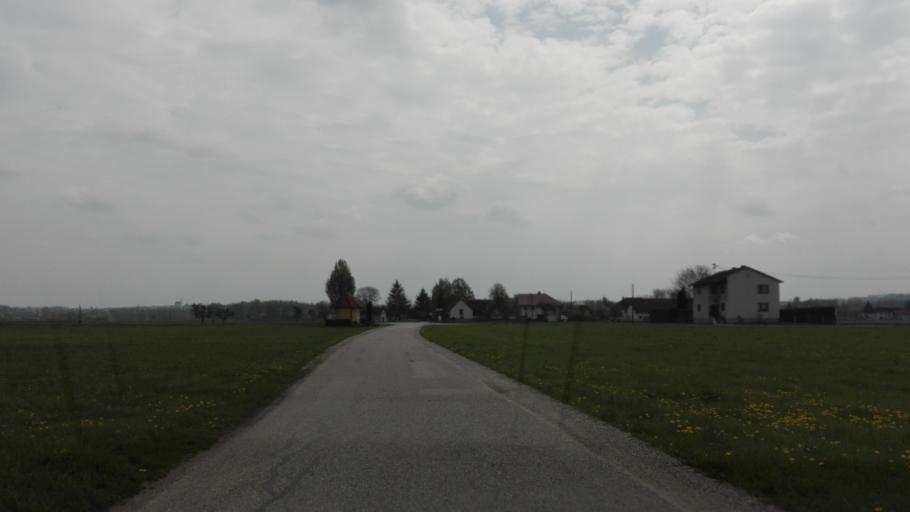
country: AT
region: Lower Austria
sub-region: Politischer Bezirk Amstetten
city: Strengberg
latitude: 48.1841
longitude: 14.6787
